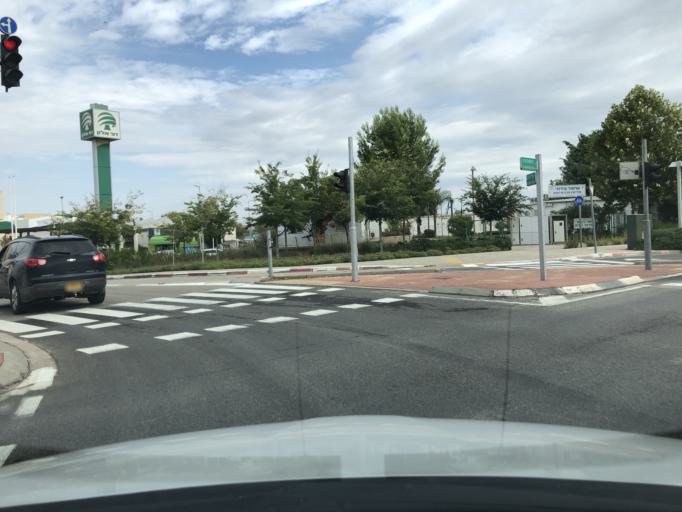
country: IL
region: Central District
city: Modiin
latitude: 31.9095
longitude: 35.0135
